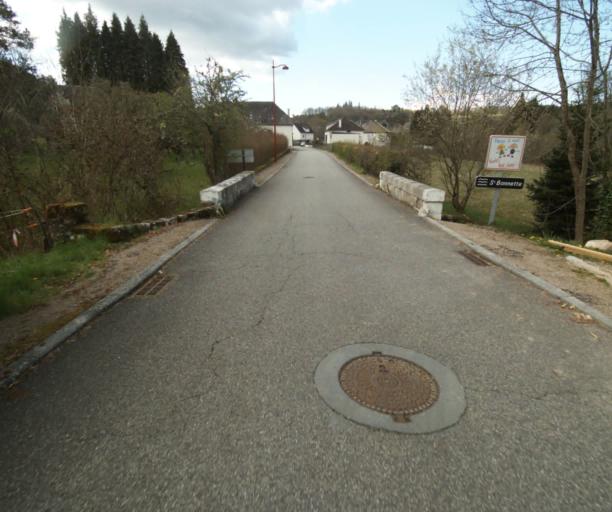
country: FR
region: Limousin
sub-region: Departement de la Correze
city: Laguenne
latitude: 45.2320
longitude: 1.8982
